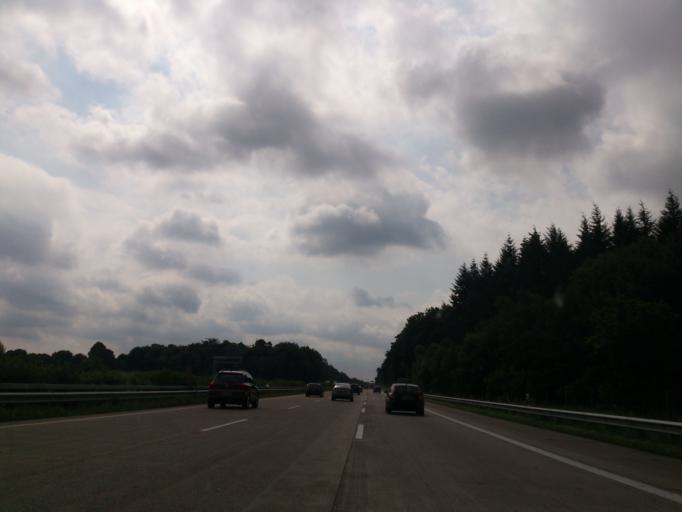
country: DE
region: Lower Saxony
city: Brackel
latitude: 53.3215
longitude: 10.0570
